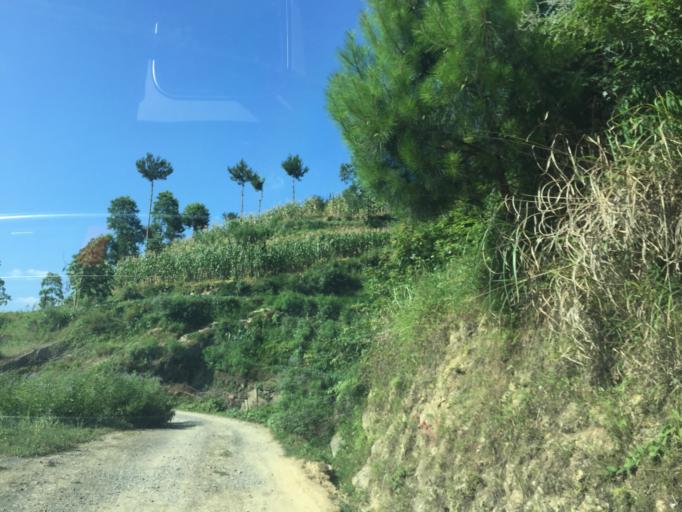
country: CN
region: Guizhou Sheng
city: Tongjing
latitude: 28.3326
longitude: 108.2952
